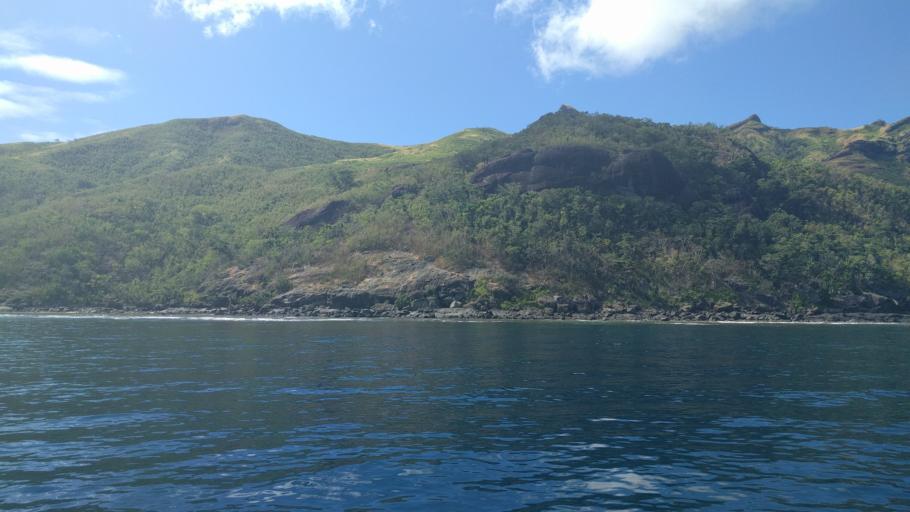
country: FJ
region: Western
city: Lautoka
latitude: -17.2879
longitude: 177.1011
